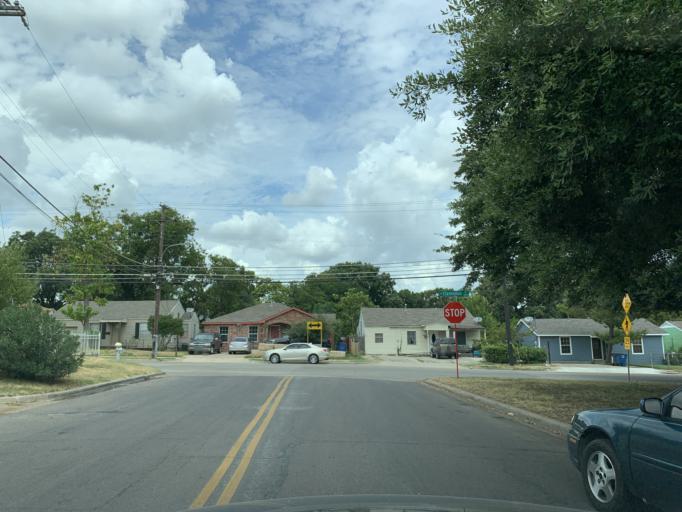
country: US
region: Texas
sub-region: Dallas County
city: Cockrell Hill
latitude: 32.7346
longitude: -96.8782
